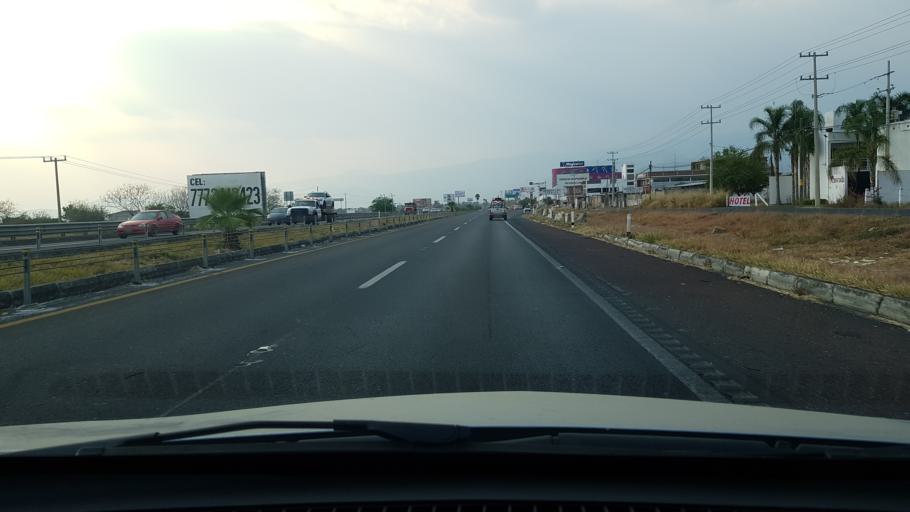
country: MX
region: Morelos
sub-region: Cuautla
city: Tierra Larga (Campo Nuevo)
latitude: 18.8625
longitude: -98.9473
